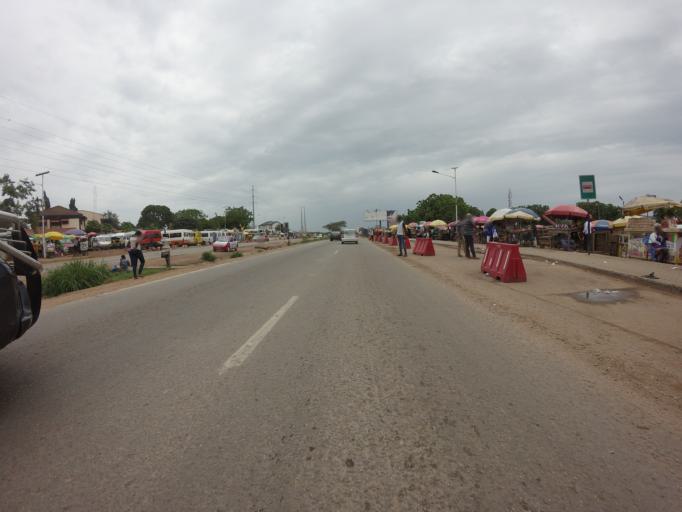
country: GH
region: Greater Accra
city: Achiaman
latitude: 5.7050
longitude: -0.2978
